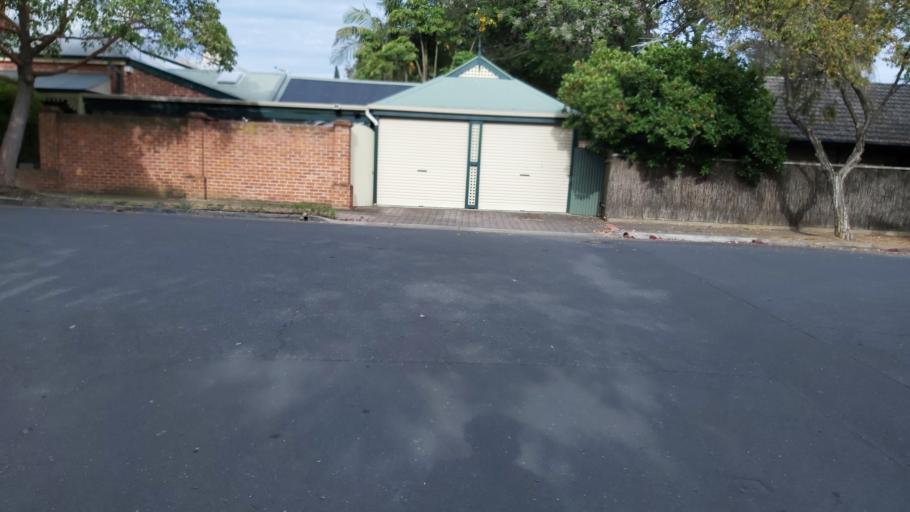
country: AU
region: South Australia
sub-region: Unley
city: Unley
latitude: -34.9531
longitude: 138.5988
